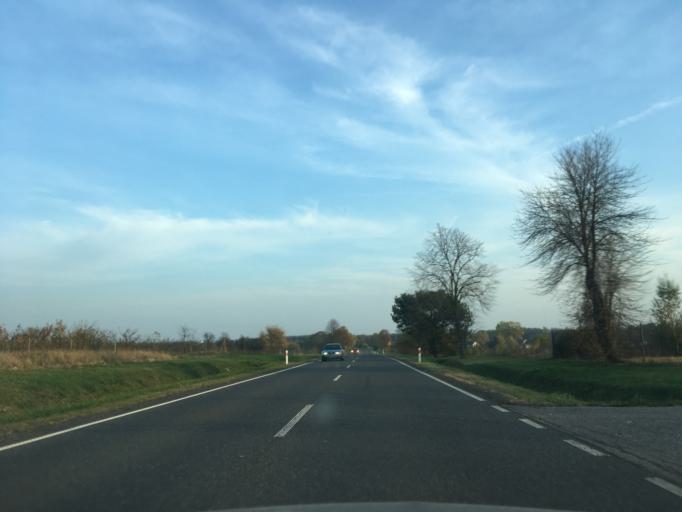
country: PL
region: Lodz Voivodeship
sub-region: Powiat skierniewicki
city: Kowiesy
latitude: 51.9225
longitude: 20.4268
